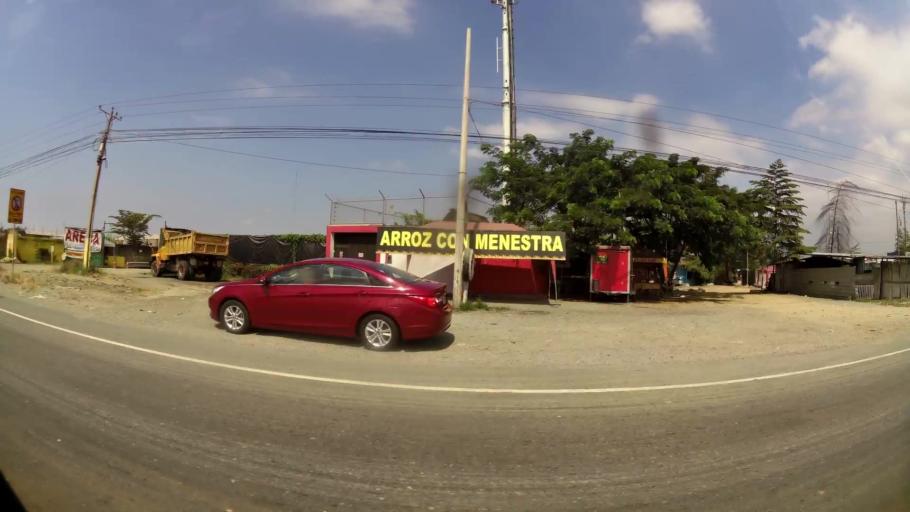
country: EC
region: Guayas
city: El Triunfo
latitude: -2.0515
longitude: -79.9143
